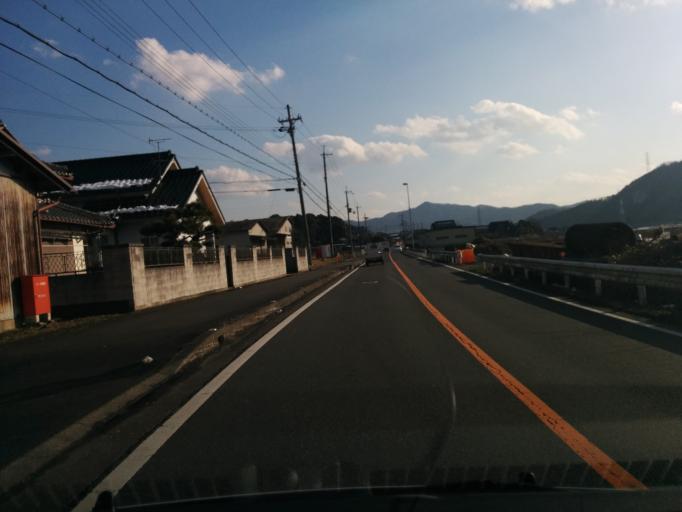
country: JP
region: Kyoto
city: Ayabe
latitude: 35.3327
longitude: 135.2154
